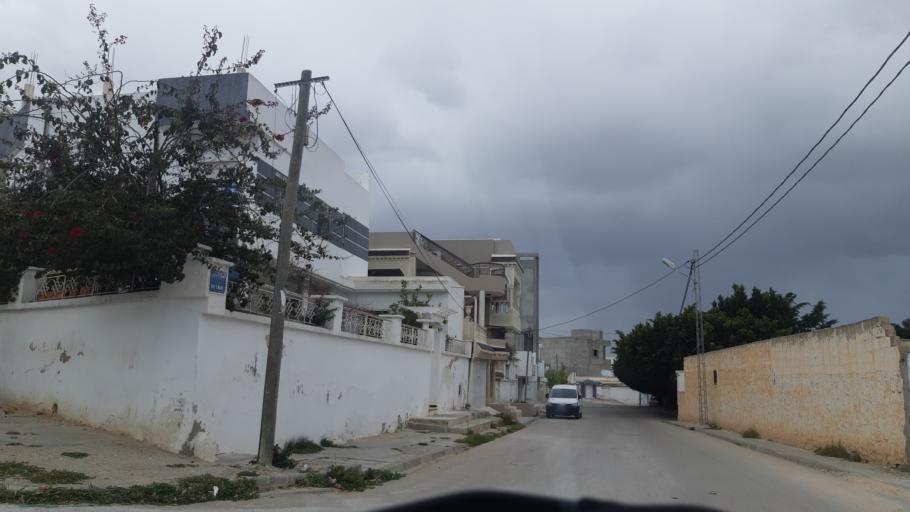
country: TN
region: Susah
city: Akouda
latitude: 35.8666
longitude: 10.5489
